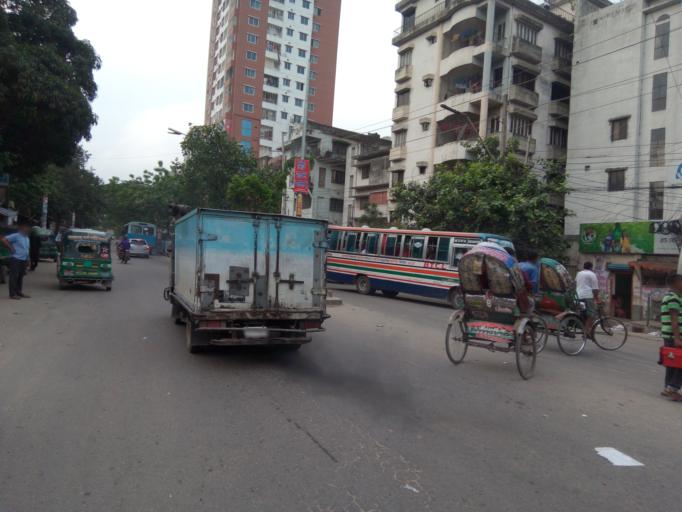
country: BD
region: Dhaka
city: Paltan
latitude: 23.7363
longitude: 90.4285
